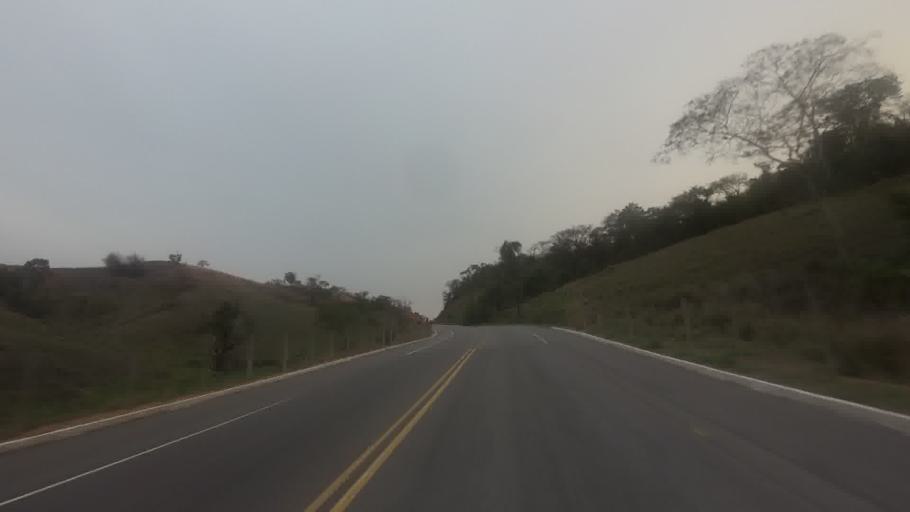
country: BR
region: Minas Gerais
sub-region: Recreio
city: Recreio
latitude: -21.7101
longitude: -42.4252
